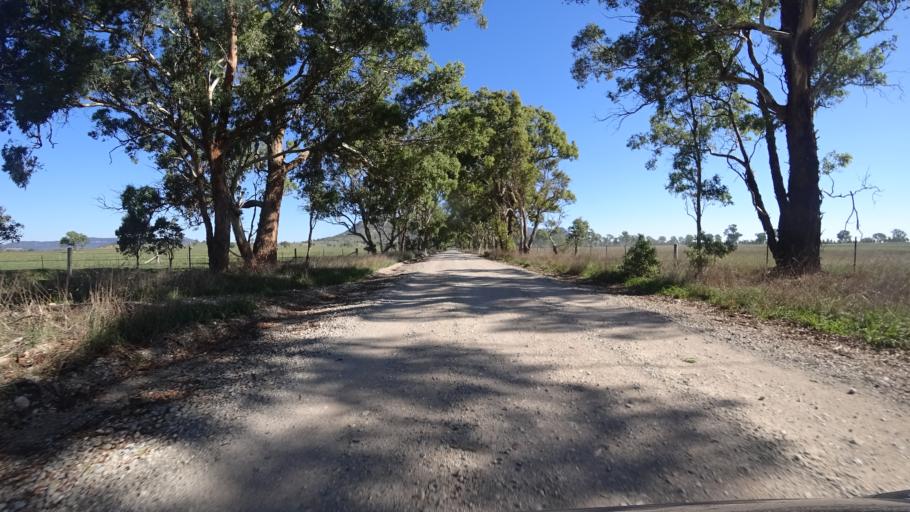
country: AU
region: New South Wales
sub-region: Mid-Western Regional
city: Kandos
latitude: -32.8244
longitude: 150.0210
